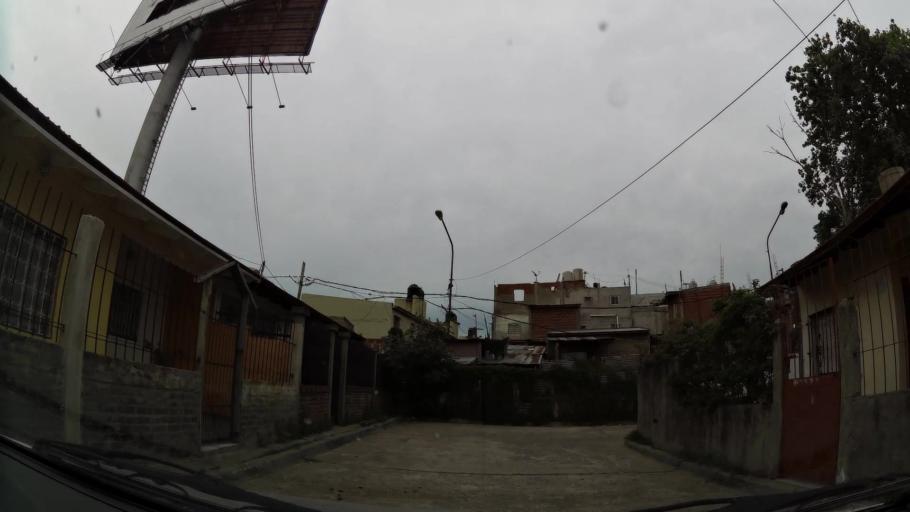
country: AR
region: Buenos Aires
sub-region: Partido de Avellaneda
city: Avellaneda
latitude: -34.6452
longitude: -58.3511
